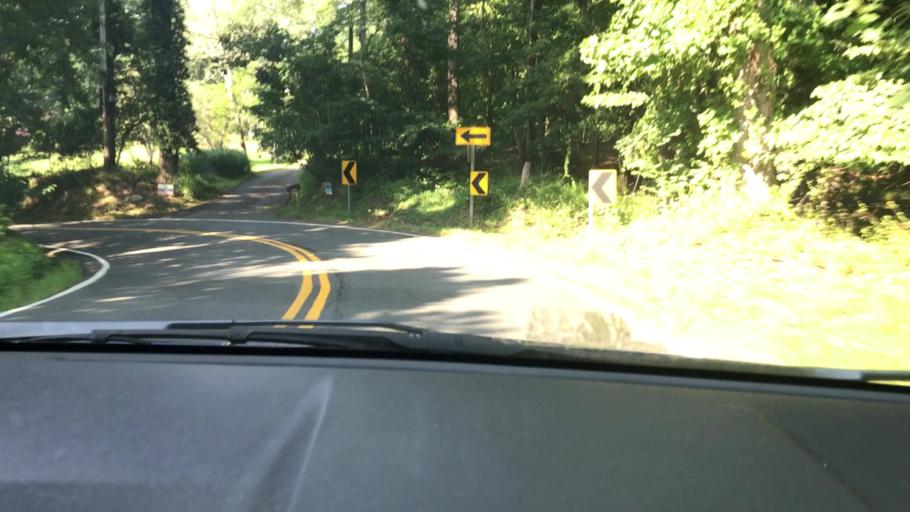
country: US
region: Virginia
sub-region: Fairfax County
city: Great Falls
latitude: 38.9872
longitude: -77.2594
